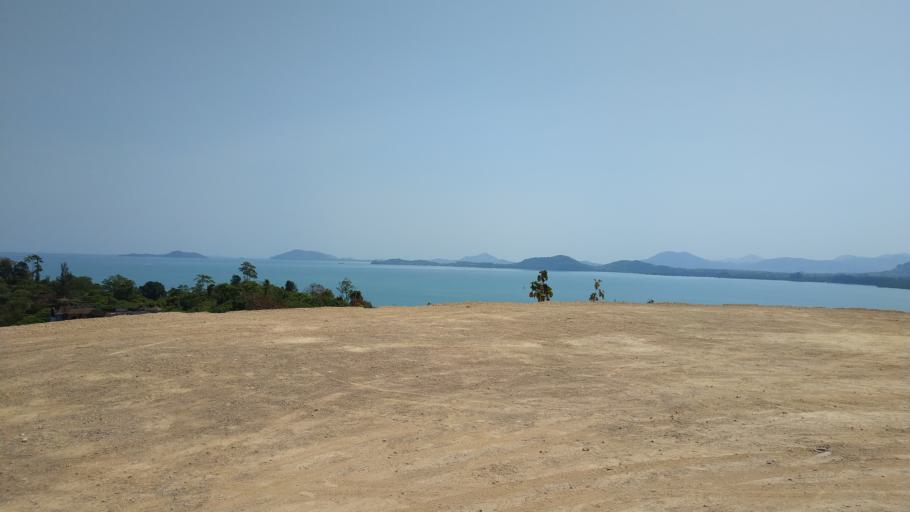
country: TH
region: Phuket
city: Thalang
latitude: 8.0437
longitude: 98.4289
